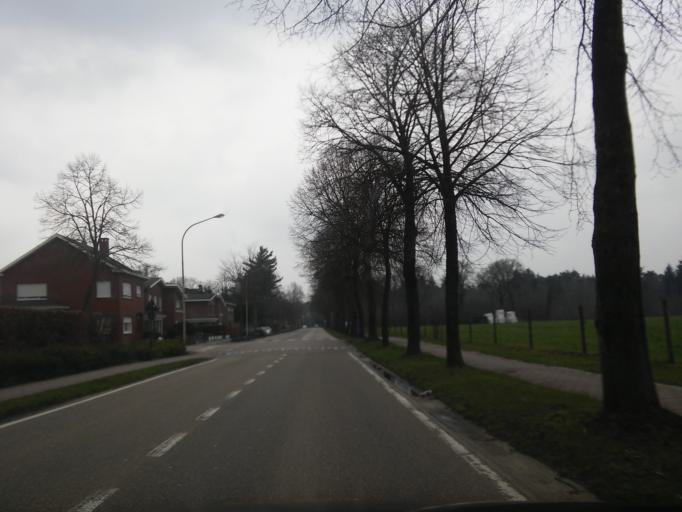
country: BE
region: Flanders
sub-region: Provincie Antwerpen
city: Grobbendonk
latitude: 51.1685
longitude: 4.7453
